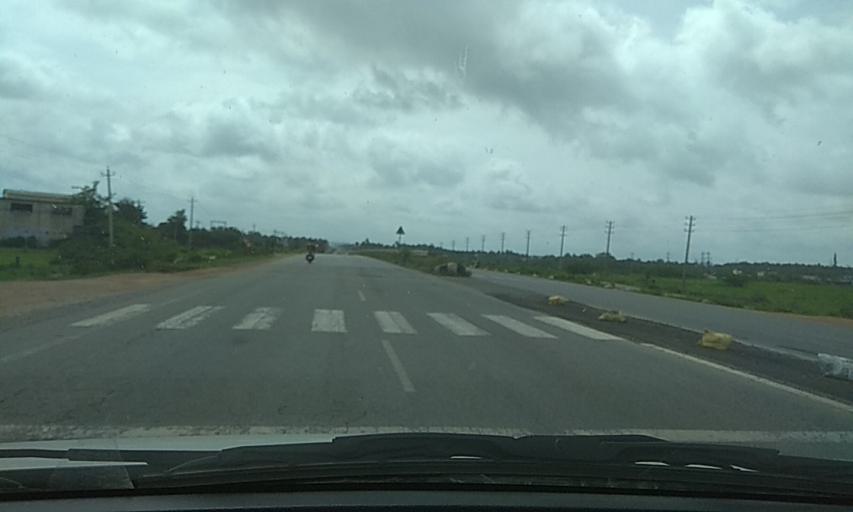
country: IN
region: Karnataka
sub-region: Davanagere
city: Harihar
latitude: 14.4549
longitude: 75.8684
